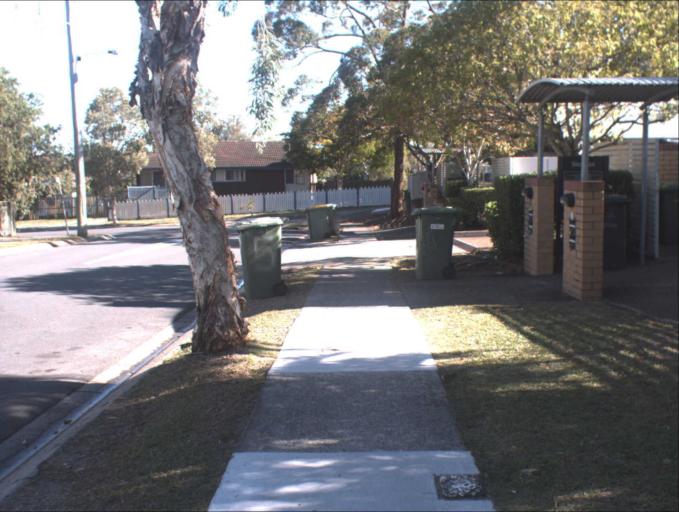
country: AU
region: Queensland
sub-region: Logan
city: Logan City
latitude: -27.6395
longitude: 153.1133
